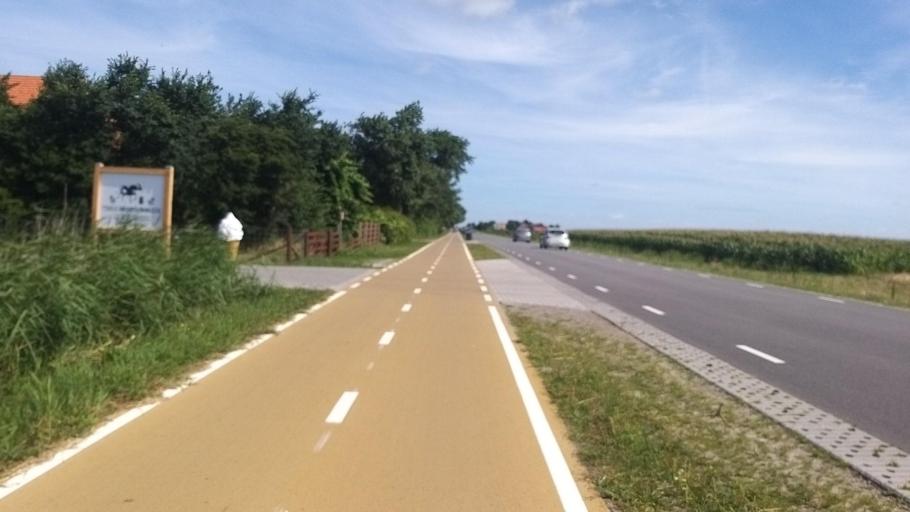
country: NL
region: North Holland
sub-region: Gemeente Texel
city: Den Burg
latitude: 53.1051
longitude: 4.8112
